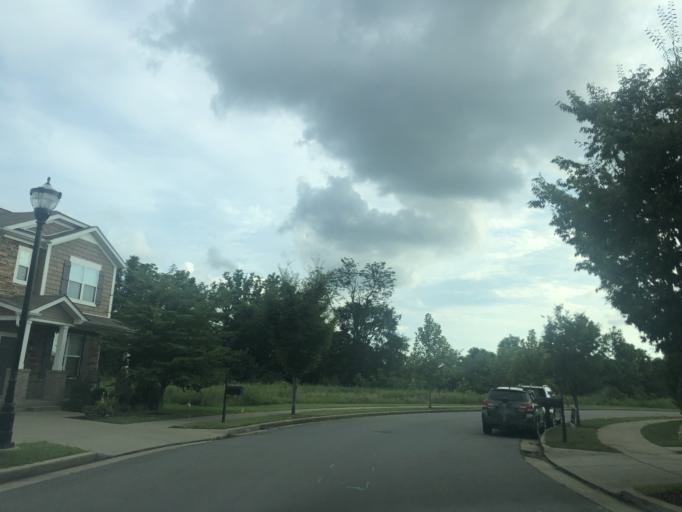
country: US
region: Tennessee
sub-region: Davidson County
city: Lakewood
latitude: 36.1641
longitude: -86.6203
